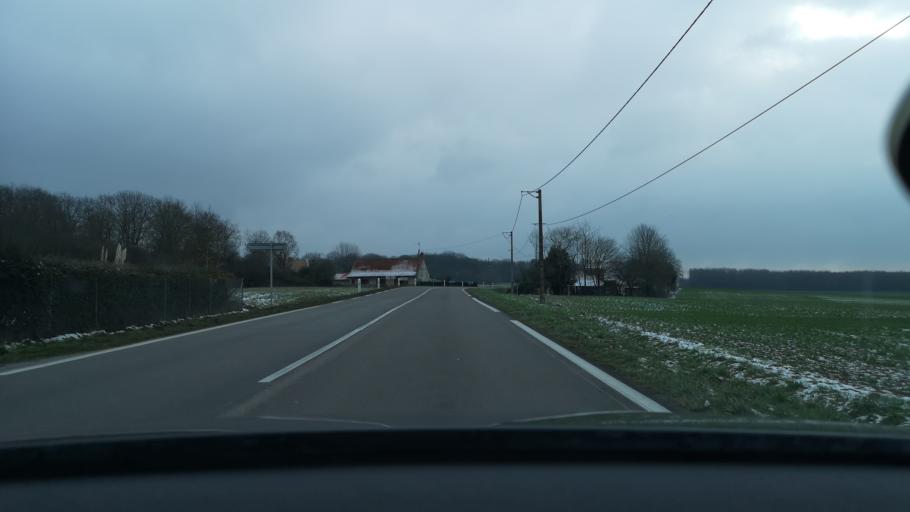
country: FR
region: Bourgogne
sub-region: Departement de Saone-et-Loire
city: Ouroux-sur-Saone
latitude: 46.7706
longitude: 4.9758
